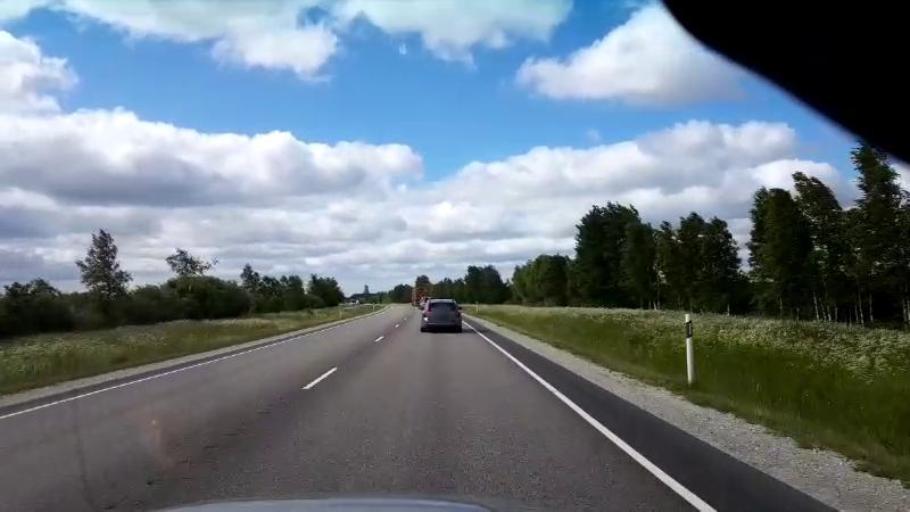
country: EE
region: Paernumaa
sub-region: Sauga vald
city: Sauga
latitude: 58.4947
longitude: 24.5327
